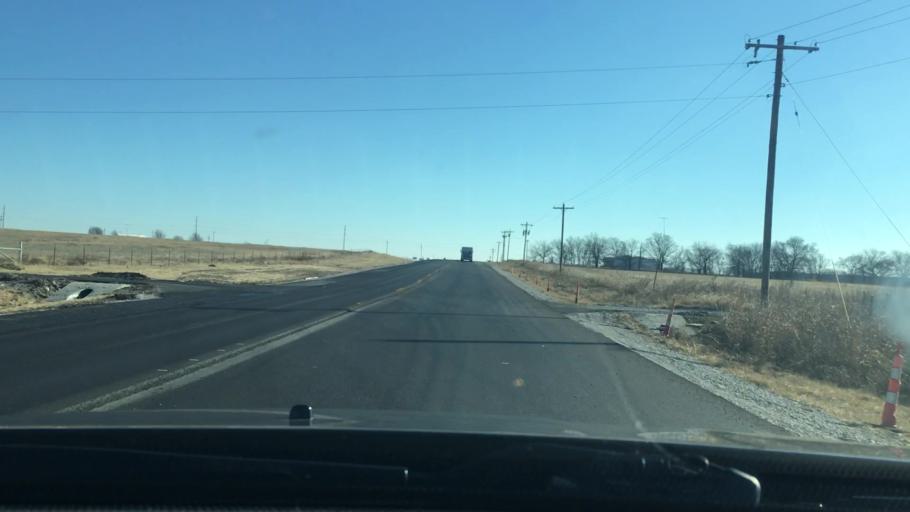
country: US
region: Oklahoma
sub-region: Love County
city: Marietta
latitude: 33.9404
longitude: -97.1479
